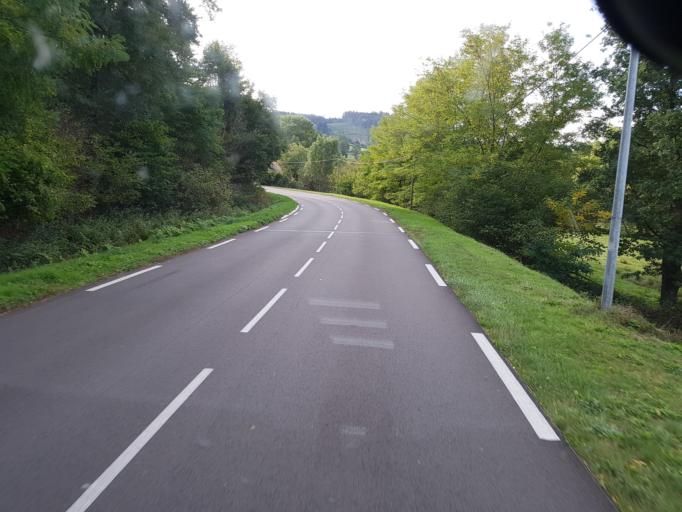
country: FR
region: Bourgogne
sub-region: Departement de Saone-et-Loire
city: La Clayette
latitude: 46.2742
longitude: 4.3734
